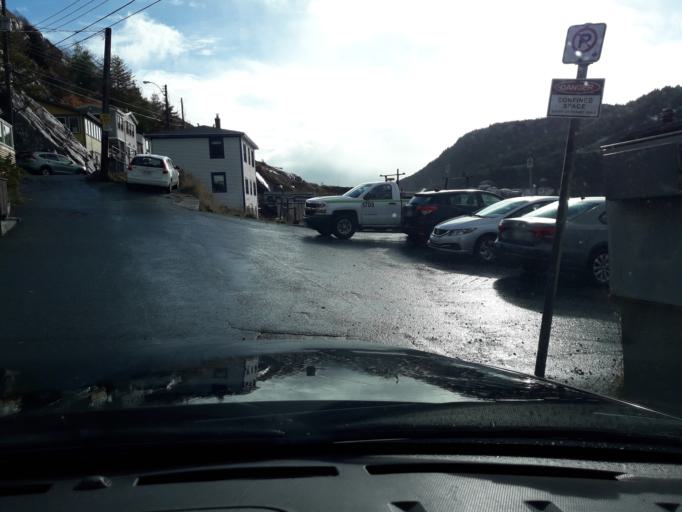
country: CA
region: Newfoundland and Labrador
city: St. John's
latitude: 47.5683
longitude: -52.6890
